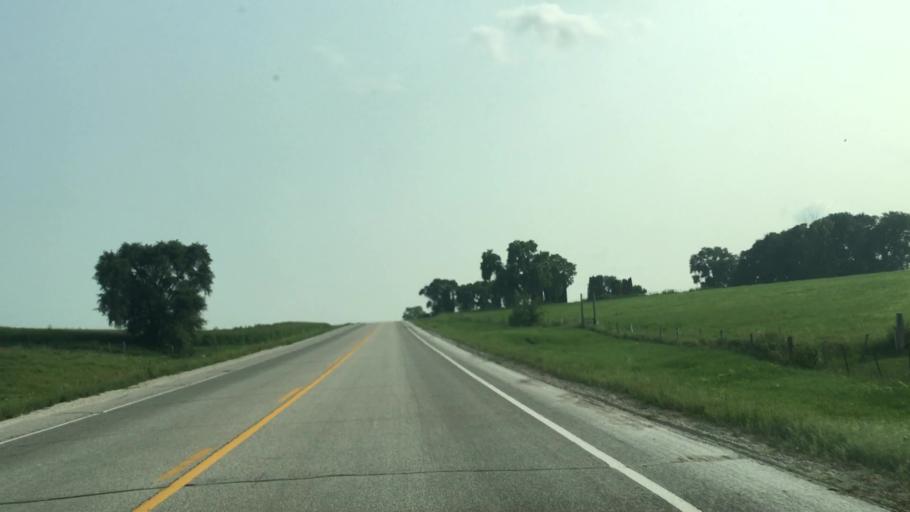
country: US
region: Minnesota
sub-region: Fillmore County
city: Harmony
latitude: 43.5423
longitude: -91.9296
